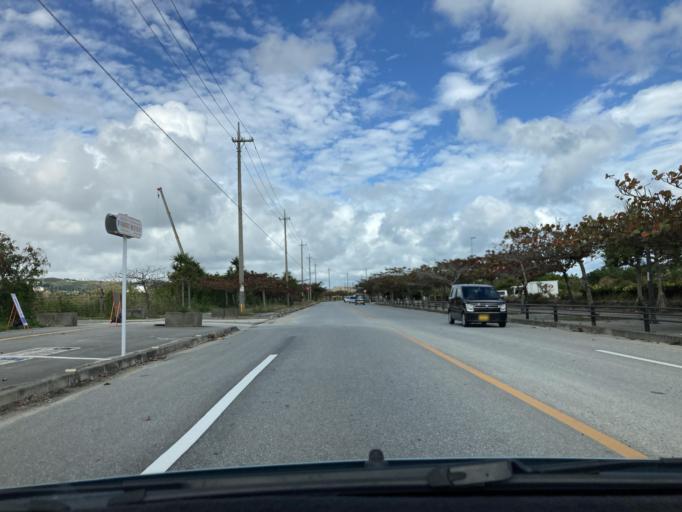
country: JP
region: Okinawa
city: Ginowan
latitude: 26.2090
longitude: 127.7668
